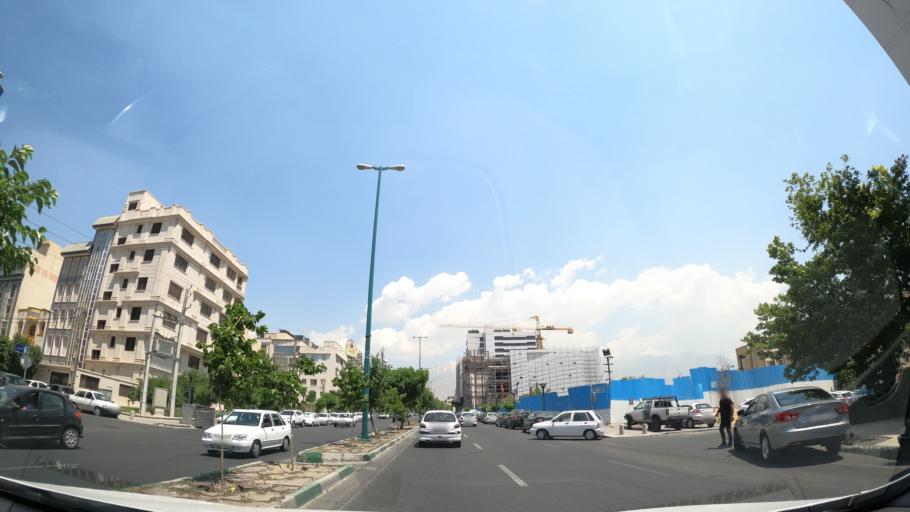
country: IR
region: Tehran
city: Tajrish
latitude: 35.7683
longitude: 51.3788
